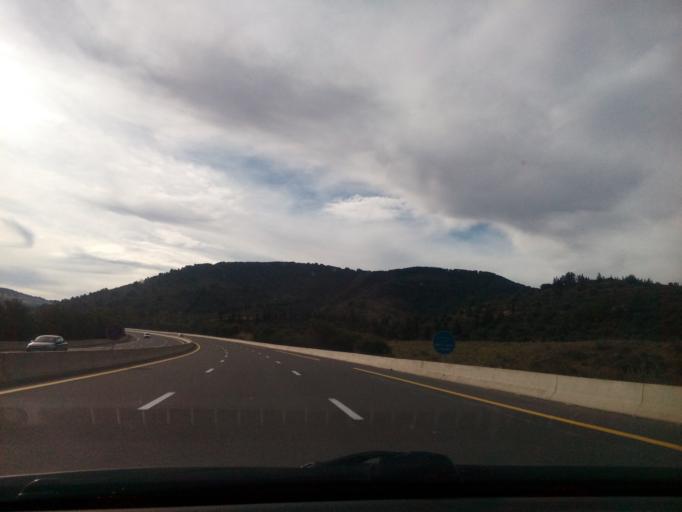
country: DZ
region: Sidi Bel Abbes
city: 'Ain el Berd
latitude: 35.4046
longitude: -0.4926
